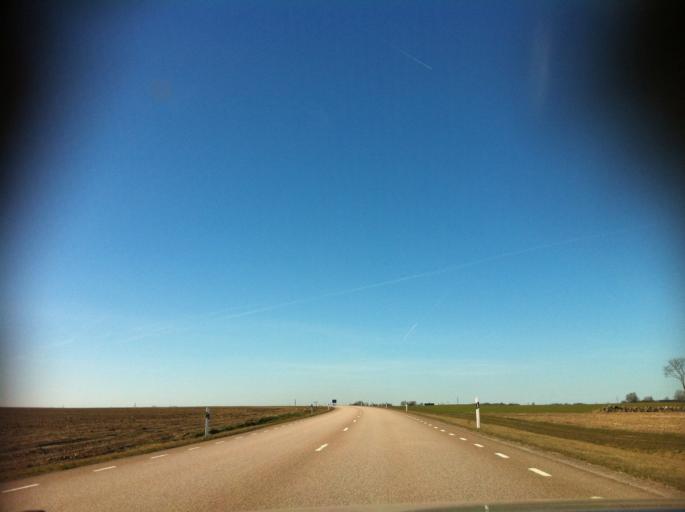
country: SE
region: Skane
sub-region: Helsingborg
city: Morarp
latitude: 56.0162
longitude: 12.8743
